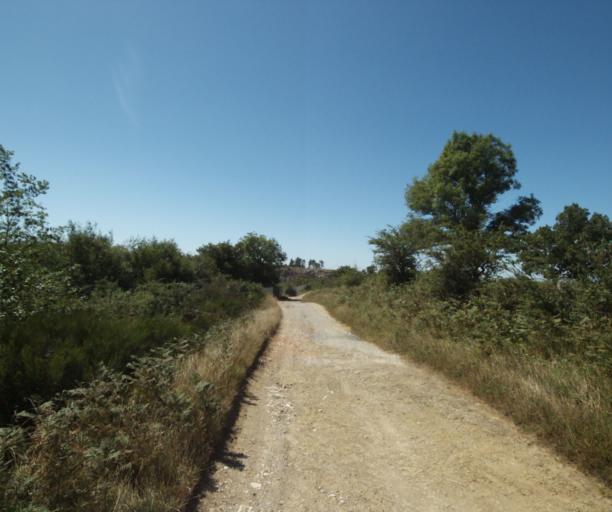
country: FR
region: Midi-Pyrenees
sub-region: Departement du Tarn
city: Soreze
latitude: 43.4434
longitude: 2.0902
